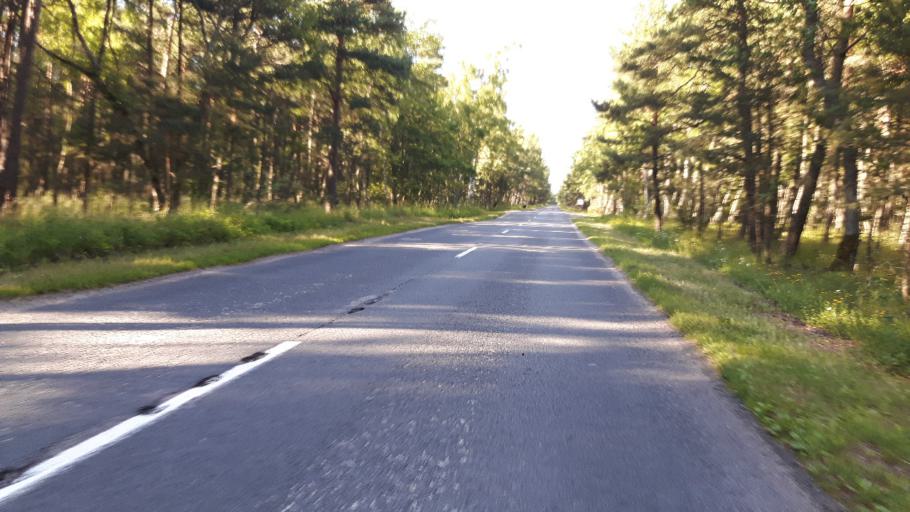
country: LT
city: Nida
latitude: 55.2062
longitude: 20.8750
